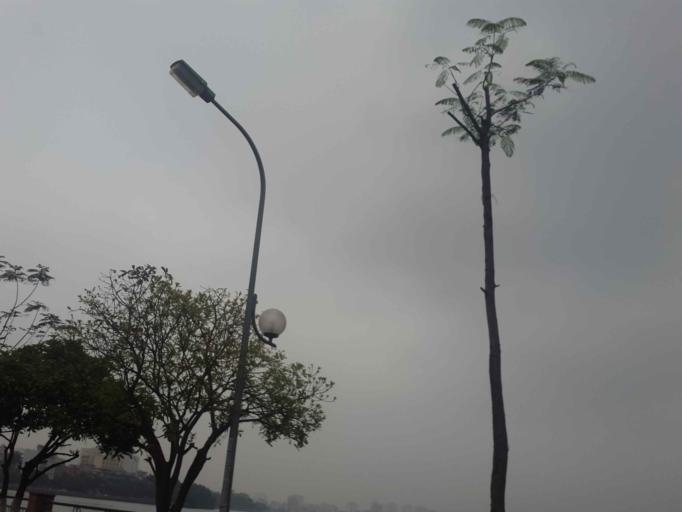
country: VN
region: Ha Noi
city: Cau Giay
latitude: 21.0448
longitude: 105.8173
